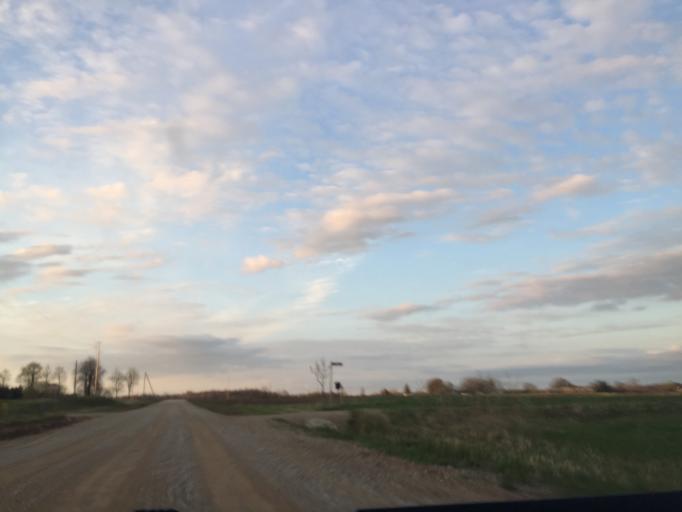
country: LV
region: Gulbenes Rajons
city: Gulbene
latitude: 57.1966
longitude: 26.7626
